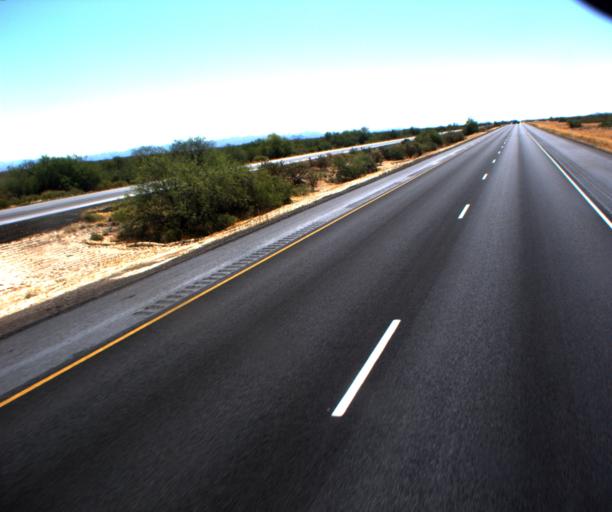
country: US
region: Arizona
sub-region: Yavapai County
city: Congress
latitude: 34.0850
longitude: -112.8960
